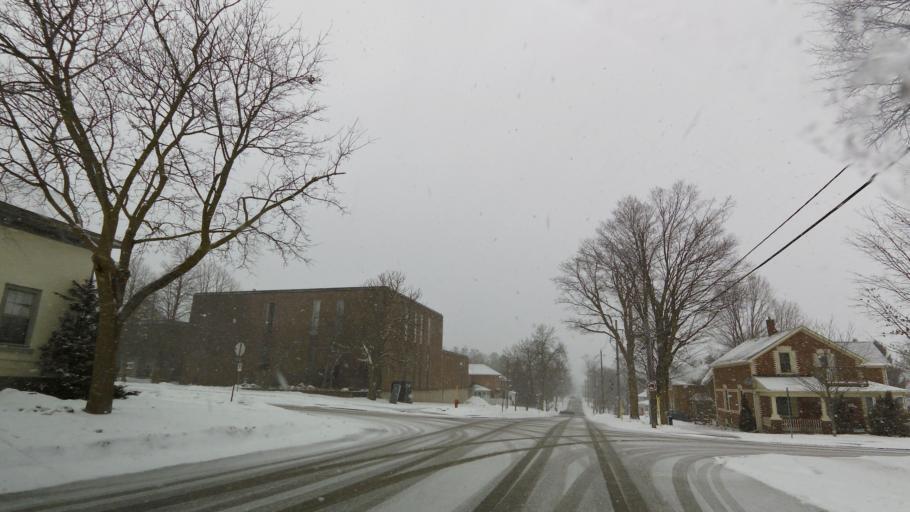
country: CA
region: Ontario
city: Orangeville
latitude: 43.9207
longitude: -80.0947
